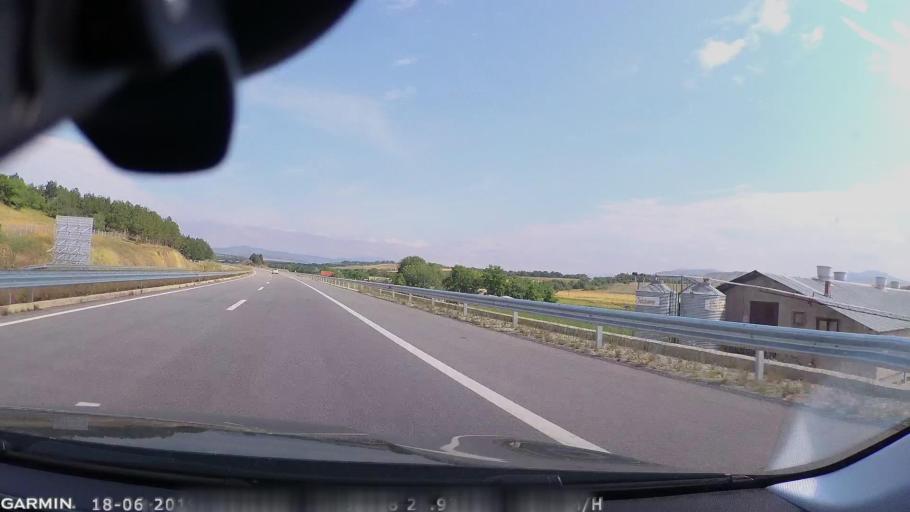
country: MK
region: Sveti Nikole
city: Sveti Nikole
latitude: 41.8849
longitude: 21.9337
